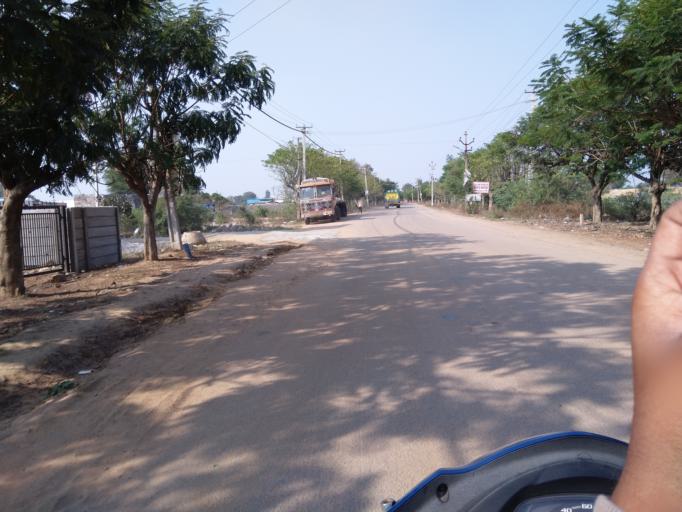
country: IN
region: Telangana
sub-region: Rangareddi
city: Quthbullapur
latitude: 17.5840
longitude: 78.4195
